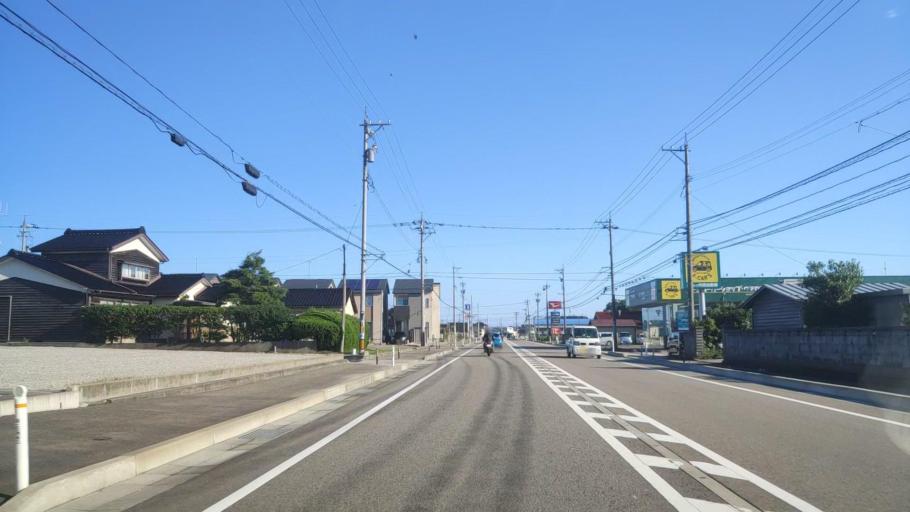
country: JP
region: Ishikawa
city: Tsubata
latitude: 36.7273
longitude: 136.6986
